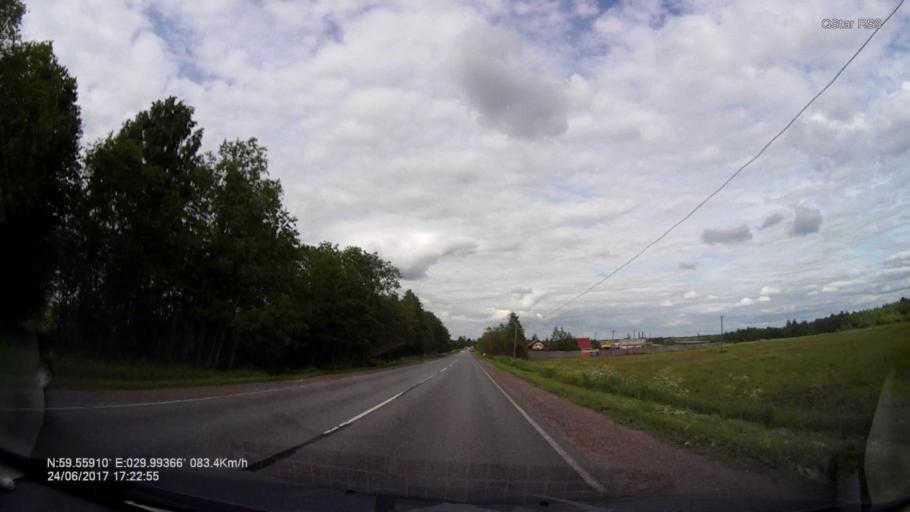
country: RU
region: Leningrad
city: Voyskovitsy
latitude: 59.5594
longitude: 29.9944
